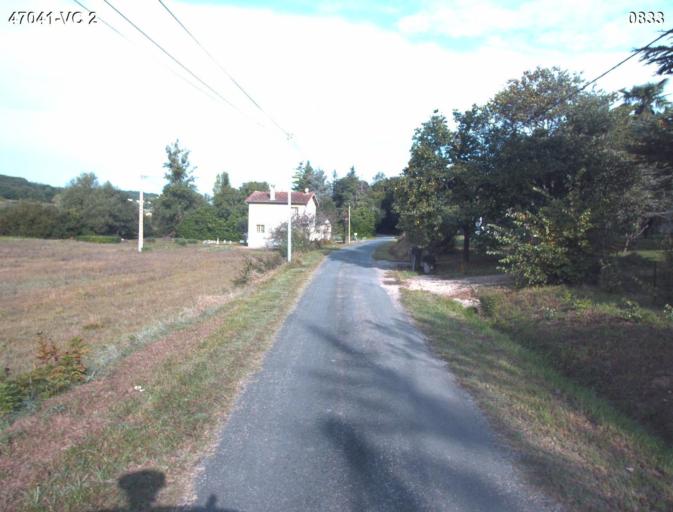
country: FR
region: Aquitaine
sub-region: Departement du Lot-et-Garonne
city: Port-Sainte-Marie
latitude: 44.1949
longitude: 0.4122
